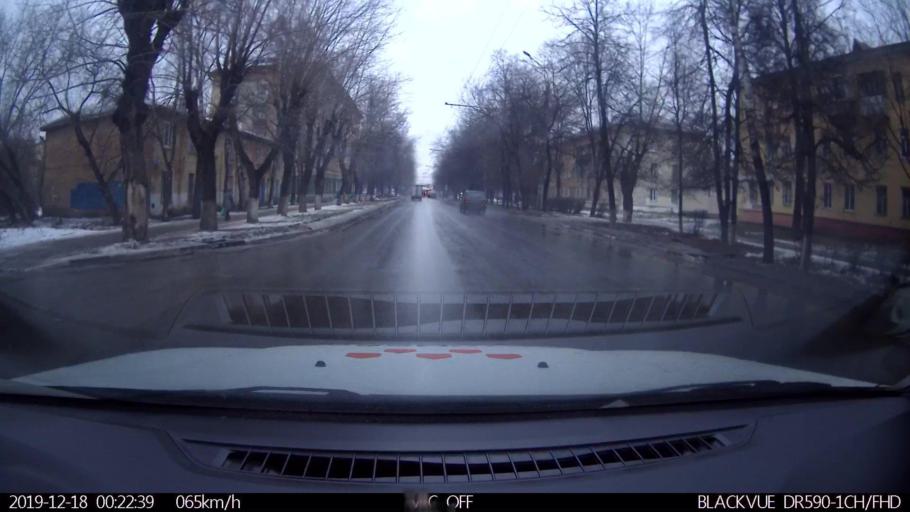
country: RU
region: Nizjnij Novgorod
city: Nizhniy Novgorod
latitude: 56.3338
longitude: 43.8855
